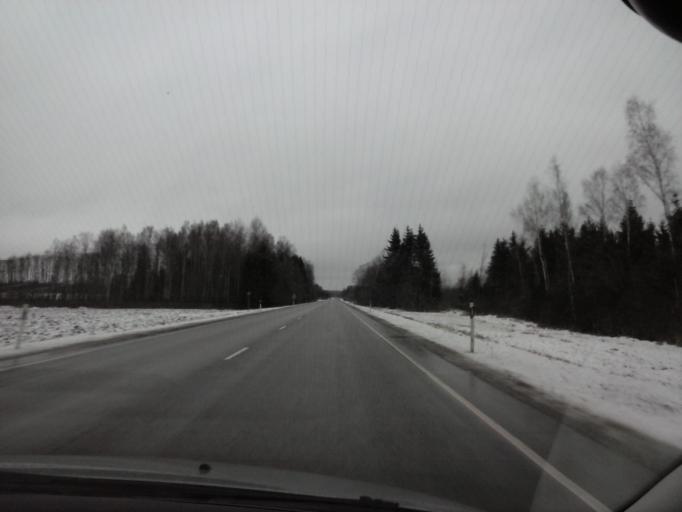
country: EE
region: Tartu
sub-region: Elva linn
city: Elva
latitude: 58.2074
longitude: 26.3594
